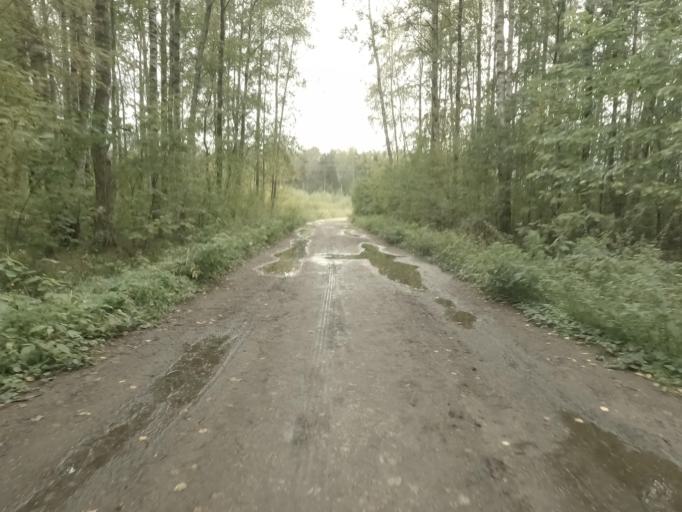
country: RU
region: St.-Petersburg
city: Krasnogvargeisky
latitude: 59.9632
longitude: 30.5014
